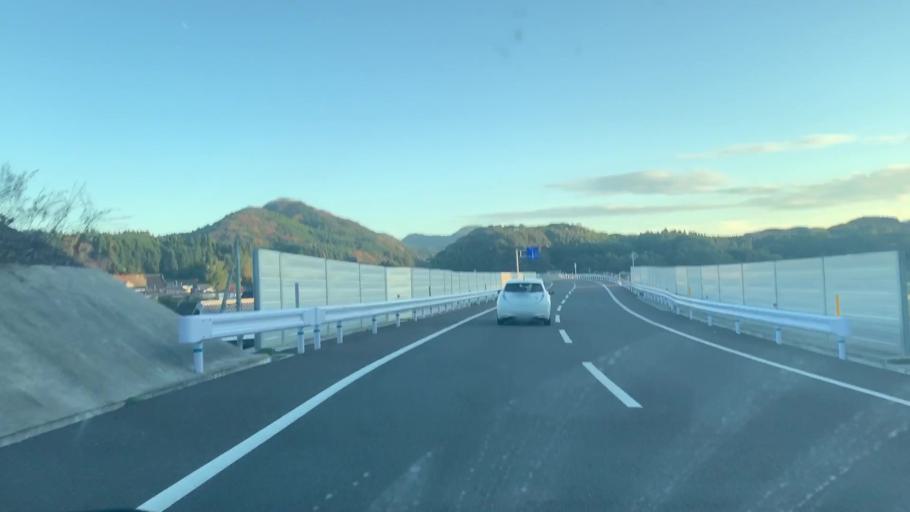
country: JP
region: Saga Prefecture
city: Takeocho-takeo
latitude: 33.2613
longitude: 129.9722
